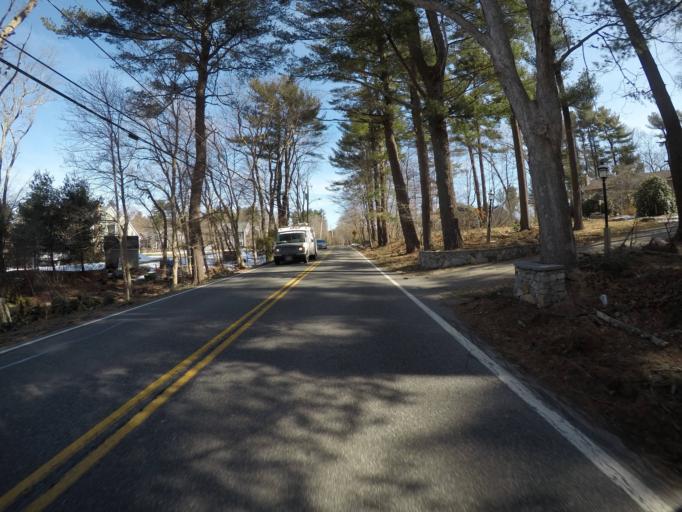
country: US
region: Massachusetts
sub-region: Bristol County
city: Easton
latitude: 41.9992
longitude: -71.1228
